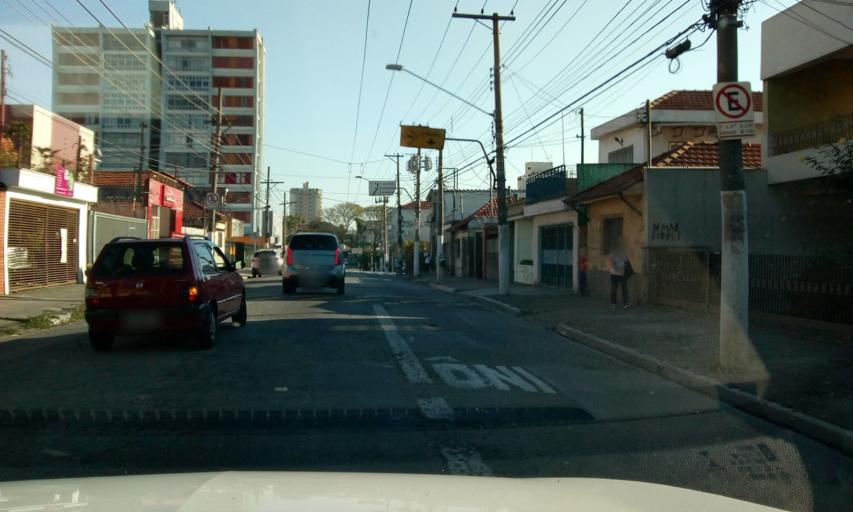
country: BR
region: Sao Paulo
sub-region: Guarulhos
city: Guarulhos
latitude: -23.5208
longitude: -46.5493
